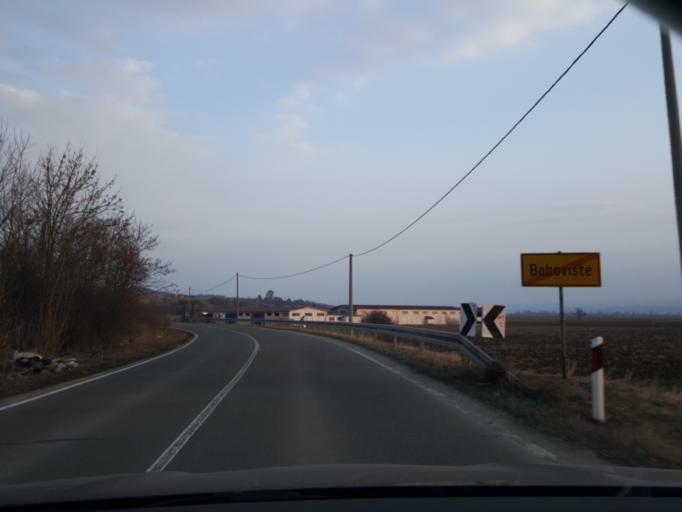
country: RS
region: Central Serbia
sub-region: Nisavski Okrug
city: Aleksinac
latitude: 43.5726
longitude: 21.6712
